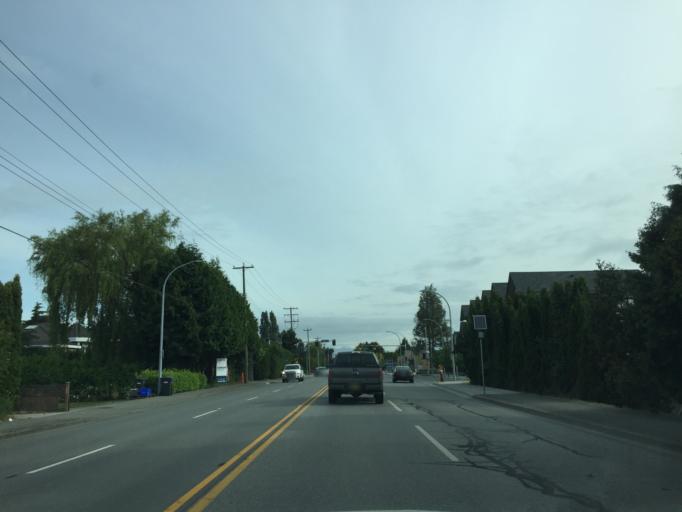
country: CA
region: British Columbia
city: Richmond
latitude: 49.1362
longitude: -123.1589
